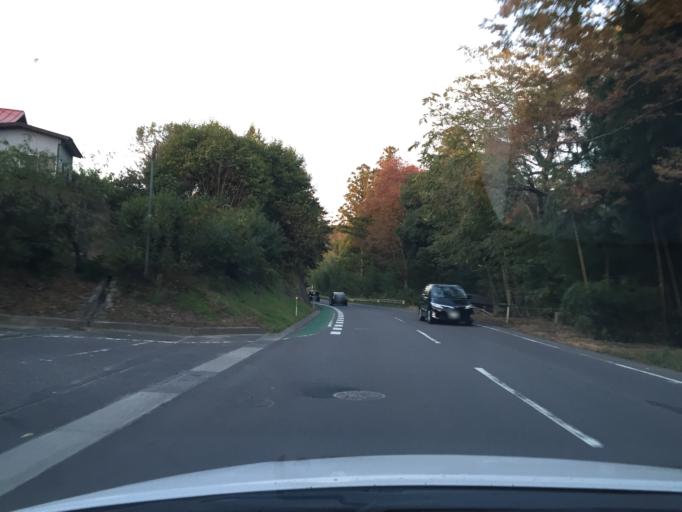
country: JP
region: Fukushima
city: Koriyama
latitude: 37.3741
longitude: 140.4453
